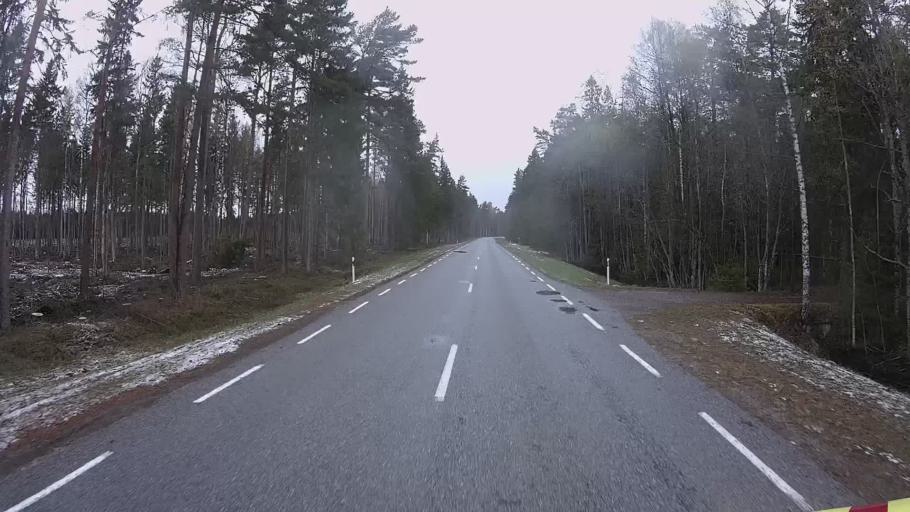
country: EE
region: Hiiumaa
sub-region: Kaerdla linn
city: Kardla
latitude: 59.0444
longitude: 22.6815
